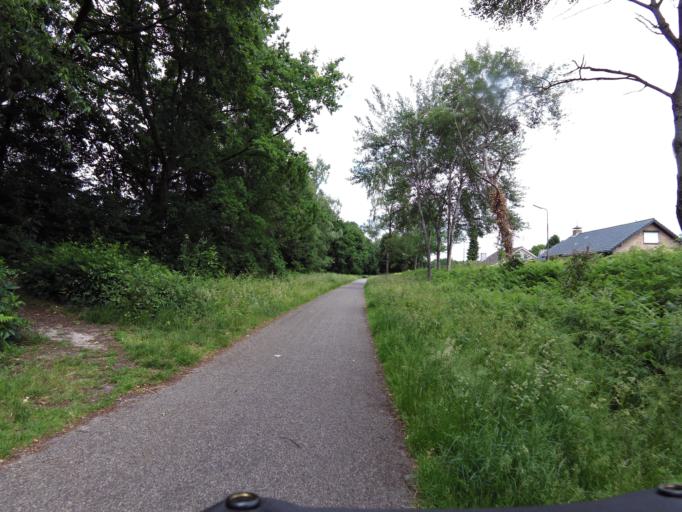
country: NL
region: North Brabant
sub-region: Gemeente Baarle-Nassau
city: Baarle-Nassau
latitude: 51.4513
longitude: 4.9274
